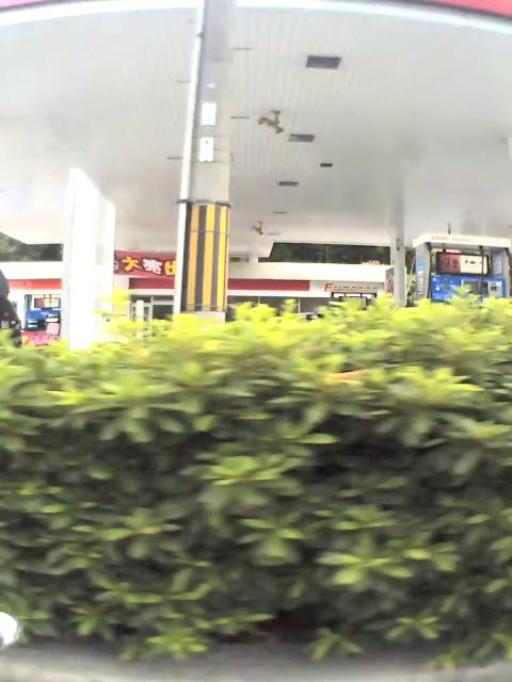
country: JP
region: Osaka
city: Hirakata
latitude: 34.8027
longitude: 135.6391
